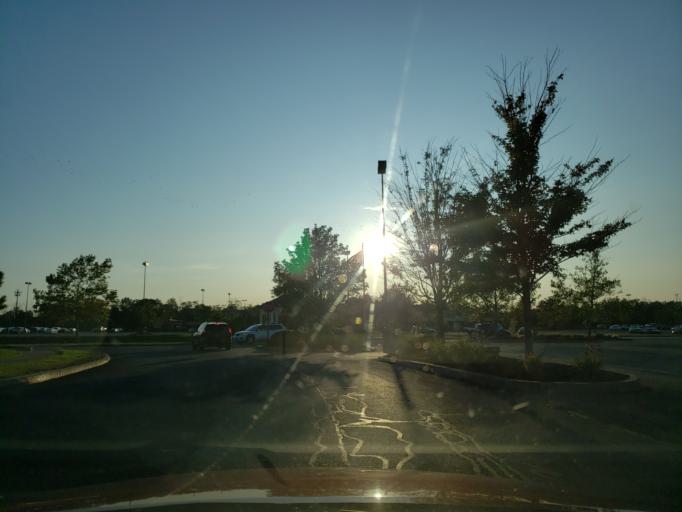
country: US
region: New York
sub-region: Monroe County
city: Webster
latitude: 43.2124
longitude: -77.4519
